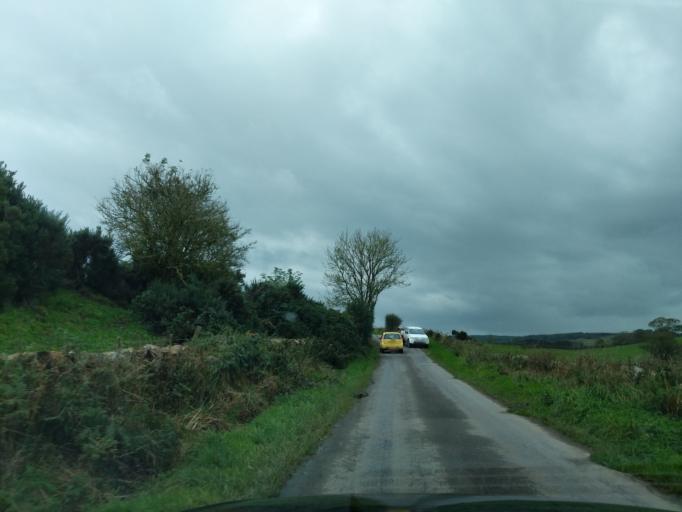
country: GB
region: Scotland
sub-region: Dumfries and Galloway
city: Castle Douglas
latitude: 54.8997
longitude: -3.9903
